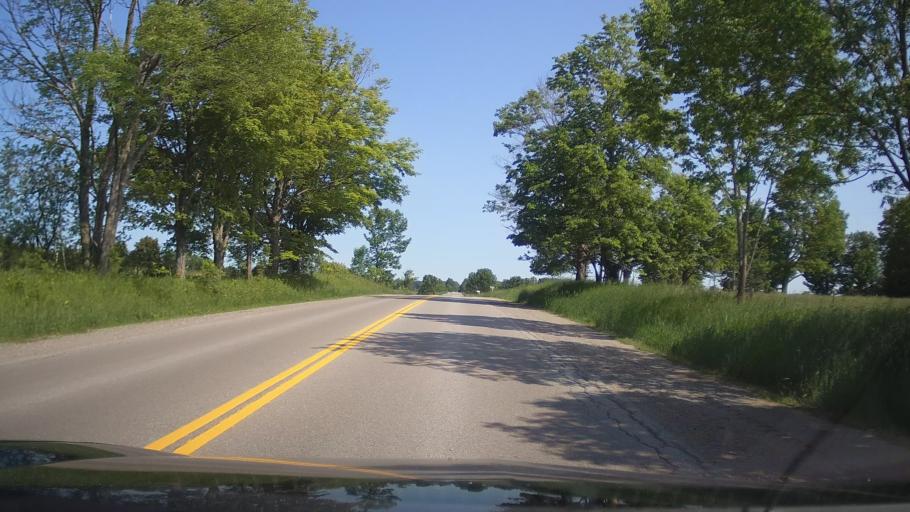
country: CA
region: Ontario
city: Uxbridge
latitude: 44.5296
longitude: -78.9646
